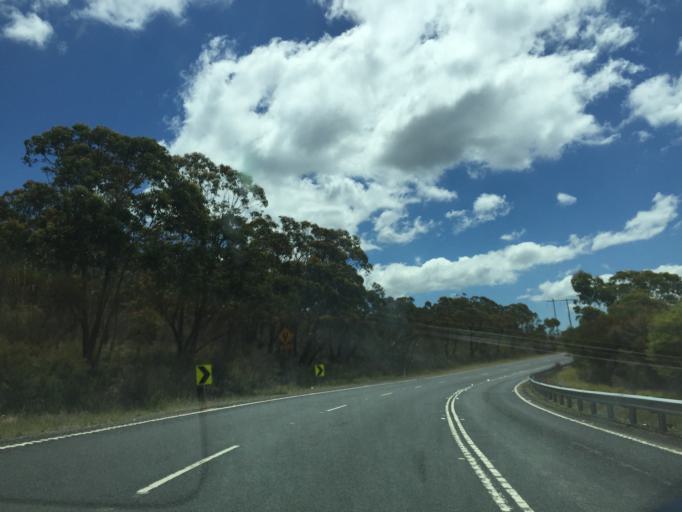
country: AU
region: New South Wales
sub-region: Blue Mountains Municipality
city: Blackheath
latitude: -33.5320
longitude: 150.3100
